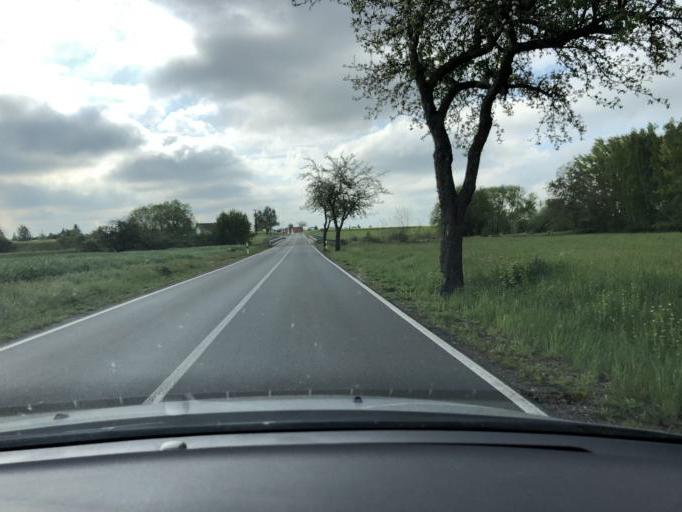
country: DE
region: Saxony
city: Regis-Breitingen
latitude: 51.0996
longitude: 12.4331
